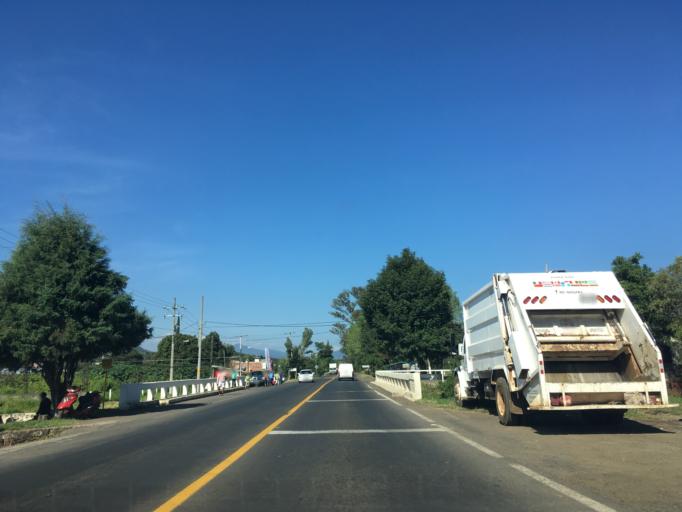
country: MX
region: Mexico
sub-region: Chalco
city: Chilchota
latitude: 19.8498
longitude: -102.1148
